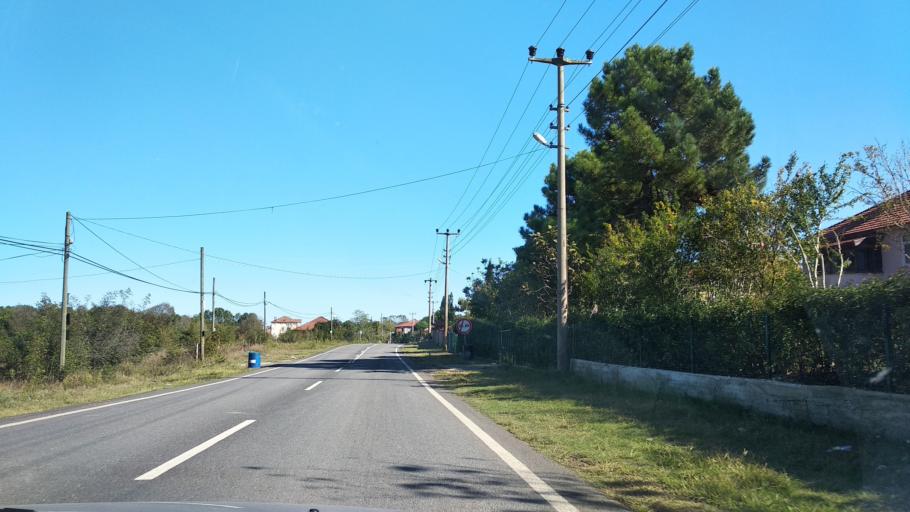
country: TR
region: Sakarya
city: Karasu
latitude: 41.1183
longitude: 30.6189
